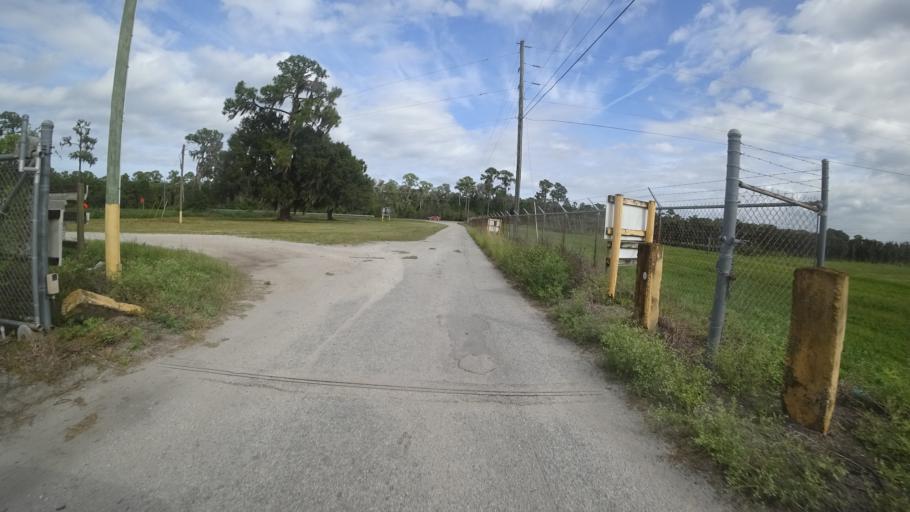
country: US
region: Florida
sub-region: Hillsborough County
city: Wimauma
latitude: 27.5963
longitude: -82.3378
